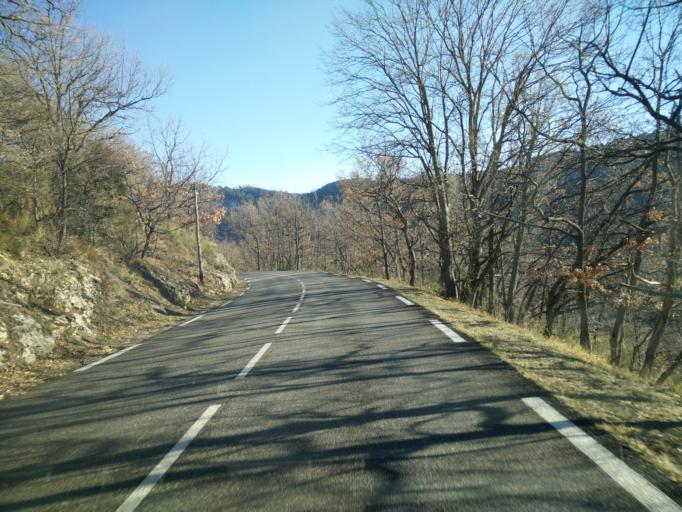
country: FR
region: Provence-Alpes-Cote d'Azur
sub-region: Departement des Alpes-Maritimes
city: Saint-Vallier-de-Thiey
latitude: 43.7173
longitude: 6.8371
